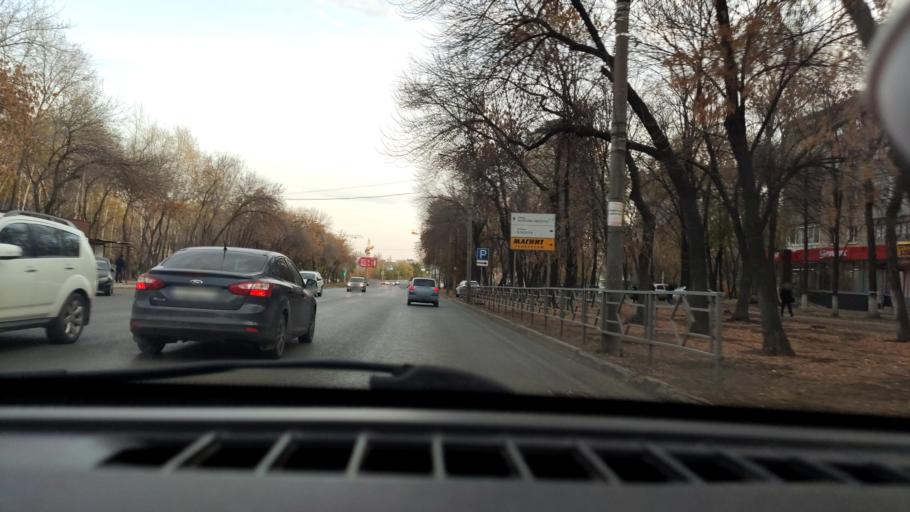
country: RU
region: Samara
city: Samara
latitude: 53.2160
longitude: 50.2097
